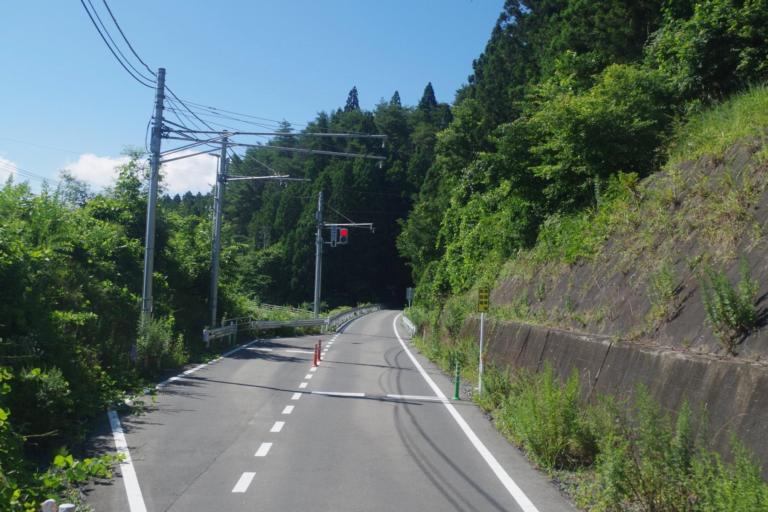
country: JP
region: Miyagi
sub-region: Oshika Gun
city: Onagawa Cho
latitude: 38.6606
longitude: 141.4466
